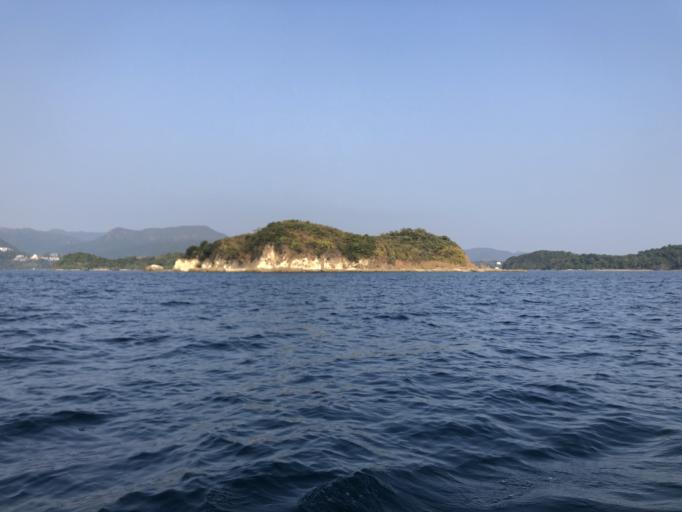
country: HK
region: Sai Kung
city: Sai Kung
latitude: 22.3730
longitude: 114.2826
